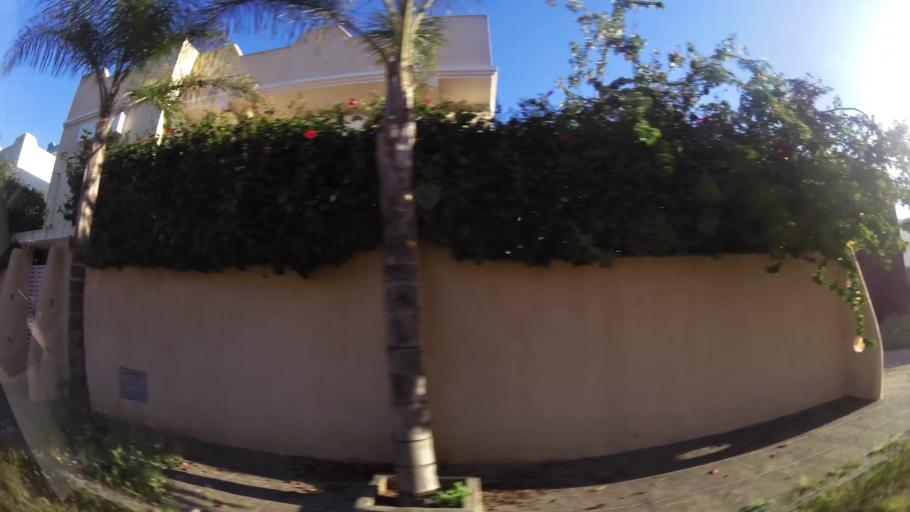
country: MA
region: Oriental
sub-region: Berkane-Taourirt
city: Madagh
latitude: 35.0888
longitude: -2.2473
